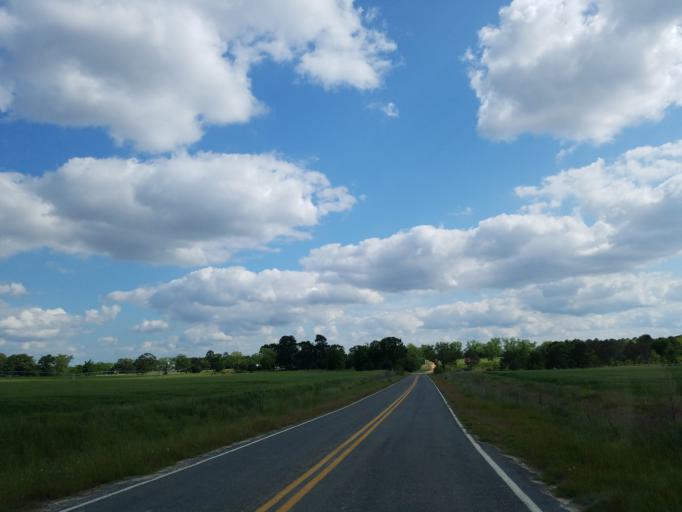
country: US
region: Georgia
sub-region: Dooly County
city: Unadilla
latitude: 32.2588
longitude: -83.7873
